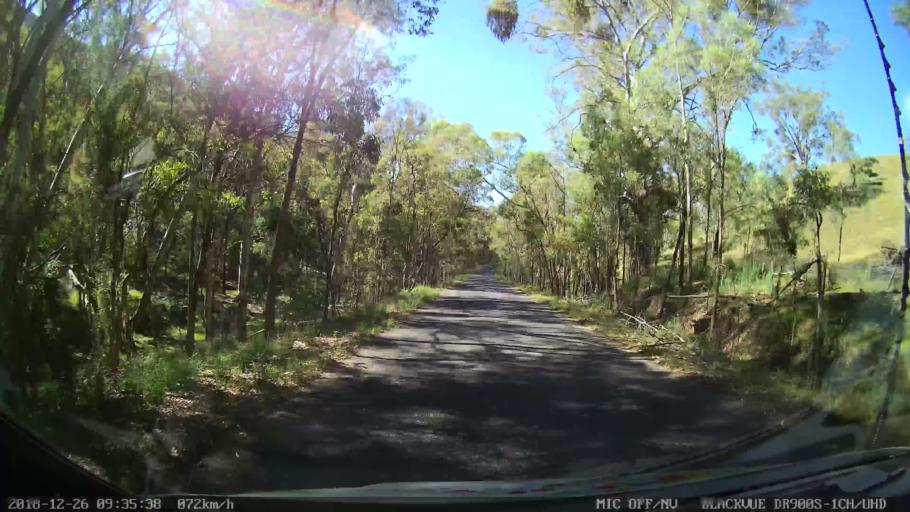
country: AU
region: New South Wales
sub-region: Mid-Western Regional
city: Kandos
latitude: -32.9164
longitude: 150.0414
